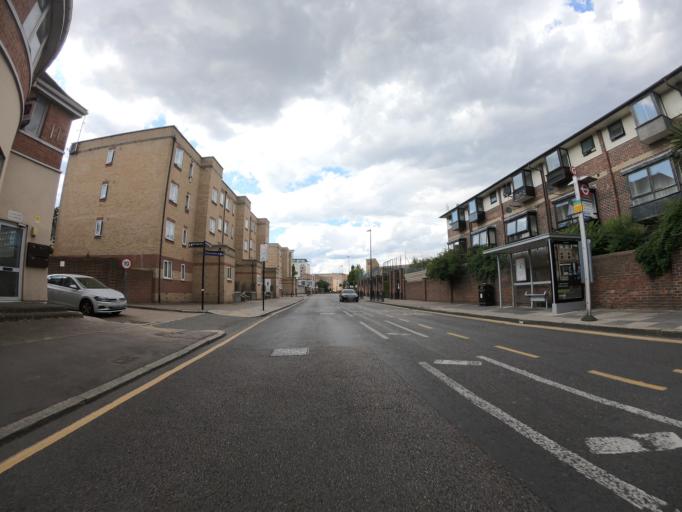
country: GB
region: England
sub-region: Greater London
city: Poplar
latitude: 51.4902
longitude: -0.0227
